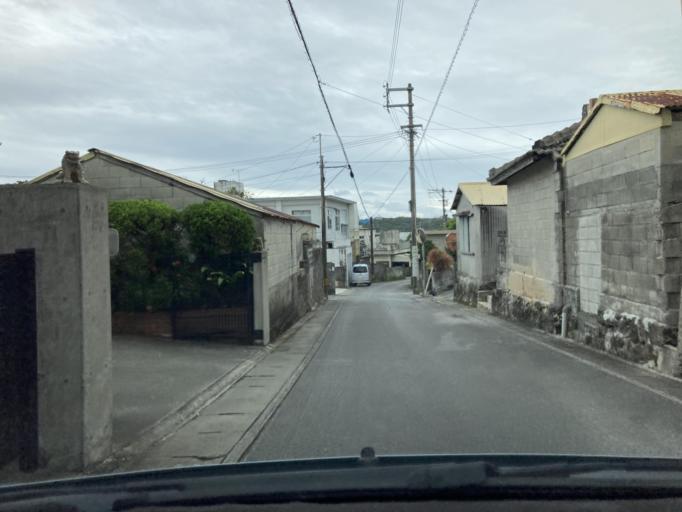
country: JP
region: Okinawa
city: Tomigusuku
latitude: 26.1751
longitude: 127.7140
